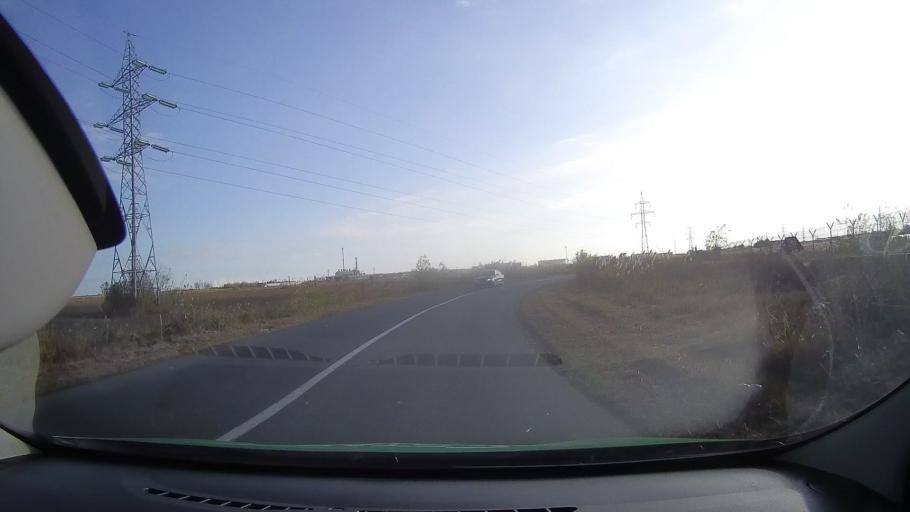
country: RO
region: Constanta
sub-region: Comuna Corbu
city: Corbu
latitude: 44.3604
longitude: 28.6759
